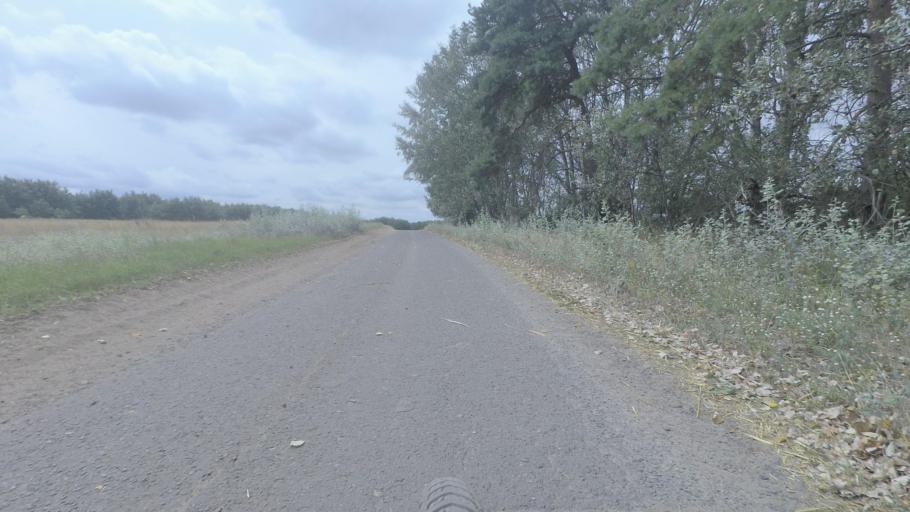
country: DE
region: Brandenburg
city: Rangsdorf
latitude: 52.2590
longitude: 13.3964
